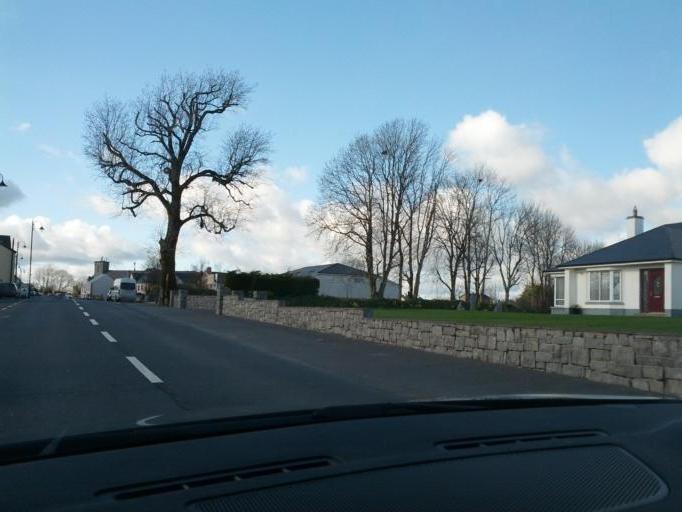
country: IE
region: Connaught
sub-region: Roscommon
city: Castlerea
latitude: 53.5523
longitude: -8.5659
